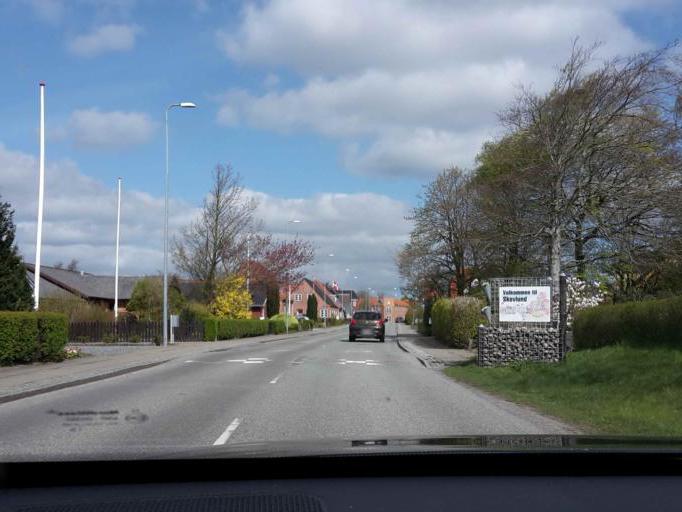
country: DK
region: South Denmark
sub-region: Varde Kommune
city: Olgod
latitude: 55.7353
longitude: 8.7101
